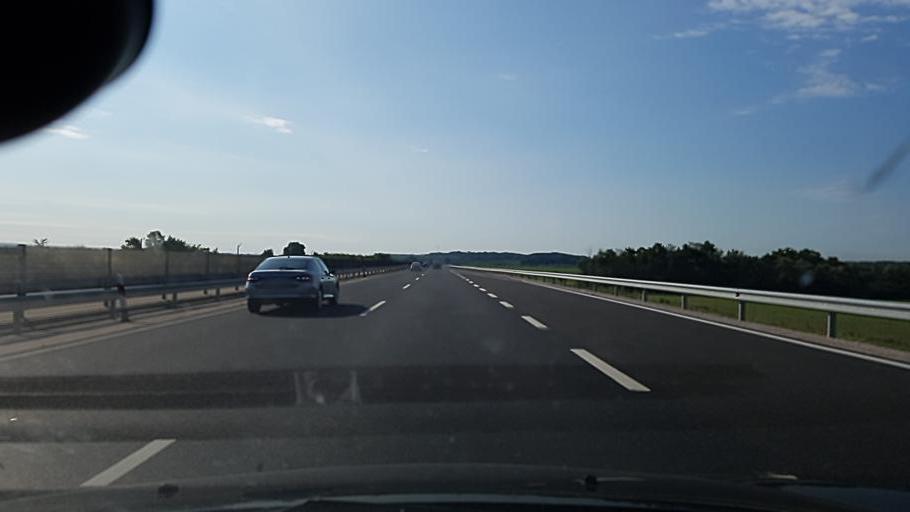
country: HU
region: Fejer
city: Adony
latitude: 47.0894
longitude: 18.8585
